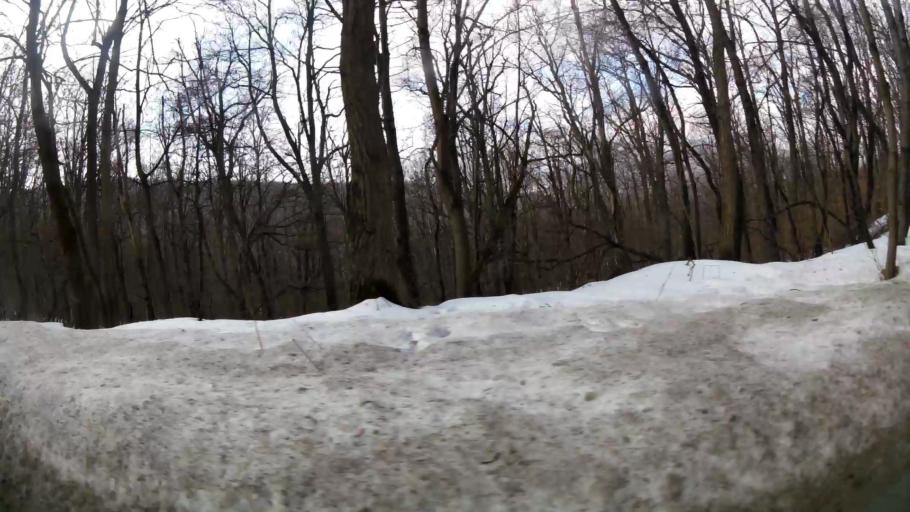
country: BG
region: Sofiya
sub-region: Obshtina Bozhurishte
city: Bozhurishte
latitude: 42.6358
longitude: 23.2220
